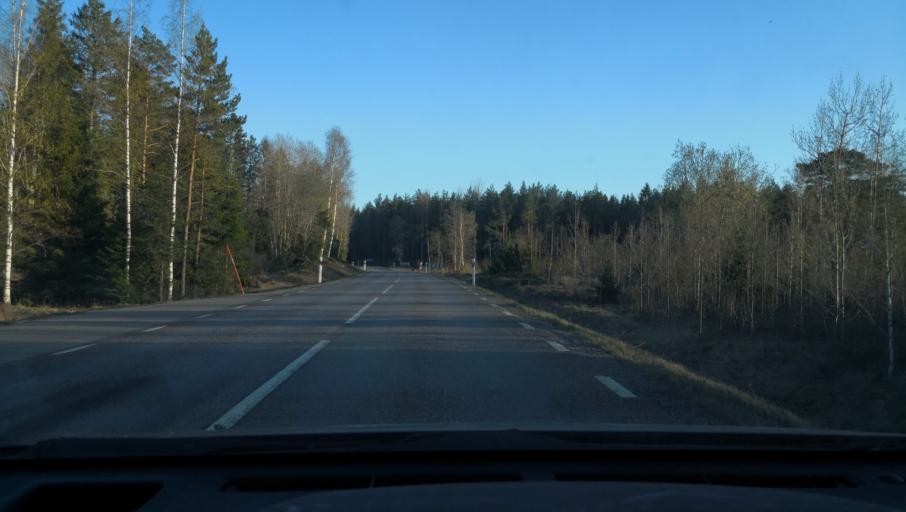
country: SE
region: Uppsala
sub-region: Enkopings Kommun
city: Irsta
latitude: 59.7792
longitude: 16.9069
